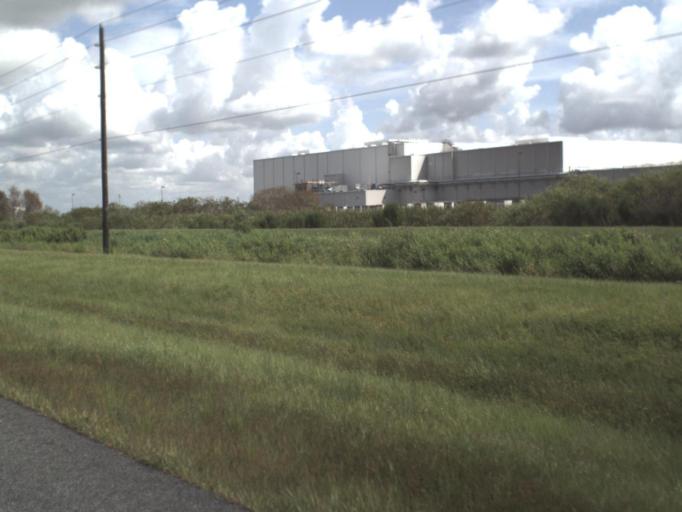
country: US
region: Florida
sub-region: Charlotte County
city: Harbour Heights
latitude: 27.0391
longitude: -81.9583
